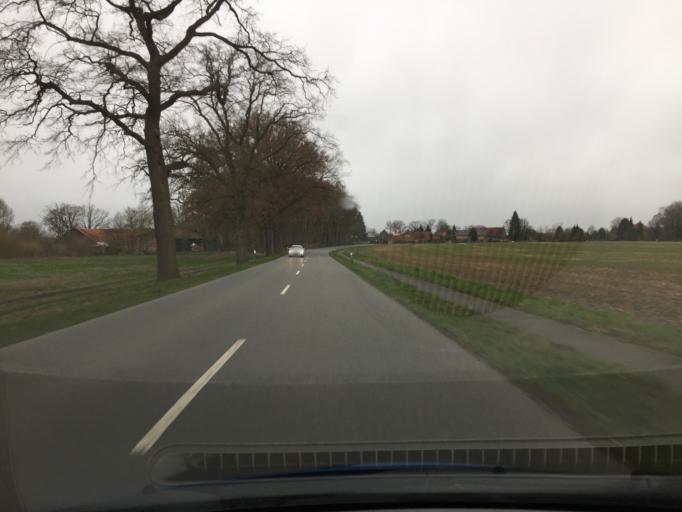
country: DE
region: Lower Saxony
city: Emmendorf
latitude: 53.0079
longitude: 10.6132
